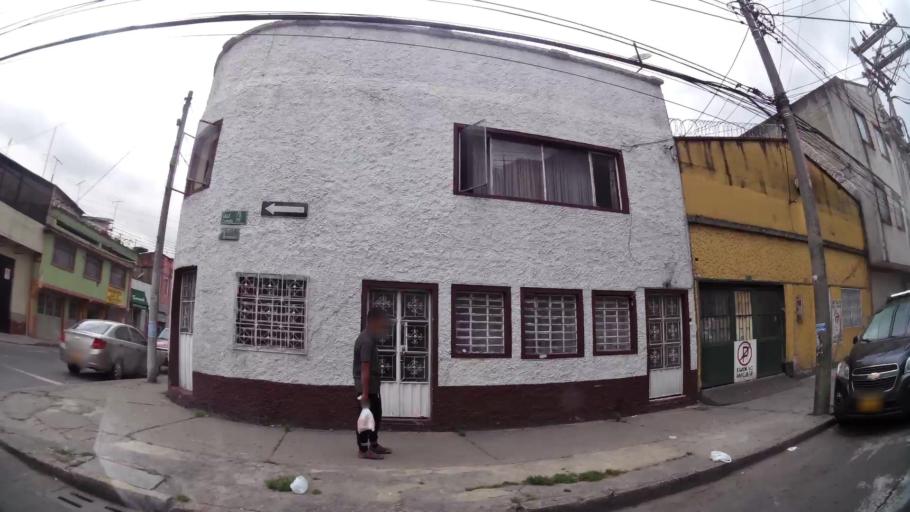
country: CO
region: Bogota D.C.
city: Barrio San Luis
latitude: 4.6671
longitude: -74.0654
